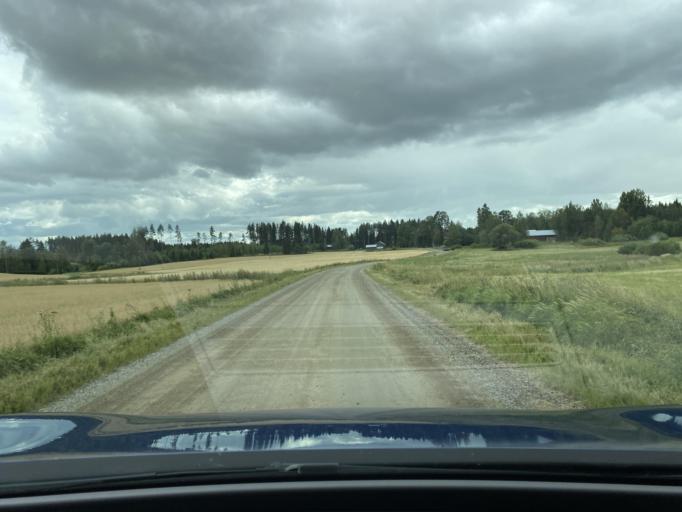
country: FI
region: Pirkanmaa
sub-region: Lounais-Pirkanmaa
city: Punkalaidun
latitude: 61.1829
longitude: 23.1847
